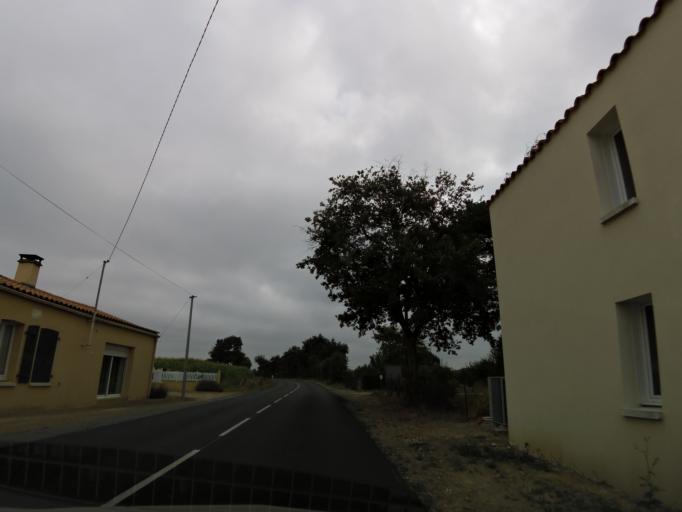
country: FR
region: Pays de la Loire
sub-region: Departement de la Vendee
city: Avrille
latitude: 46.4719
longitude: -1.4491
